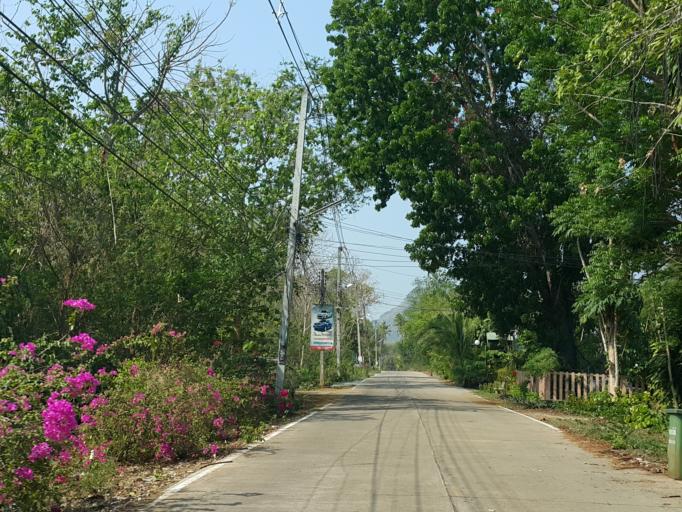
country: TH
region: Kanchanaburi
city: Sai Yok
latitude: 14.1173
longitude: 99.1379
